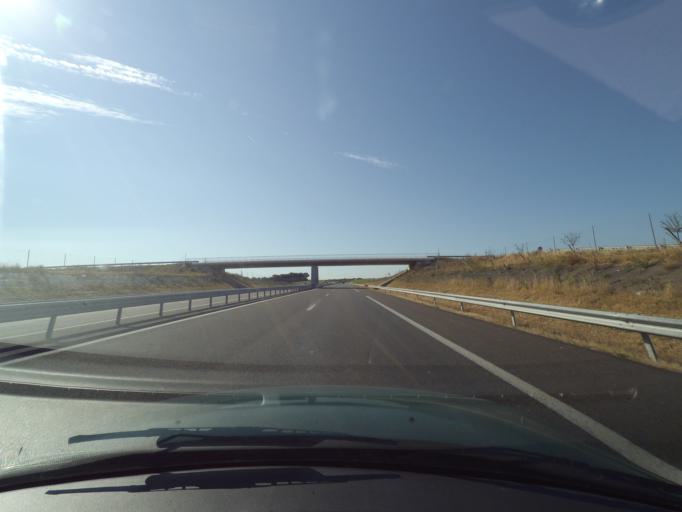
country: FR
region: Poitou-Charentes
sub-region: Departement de la Vienne
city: Terce
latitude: 46.4733
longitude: 0.5416
